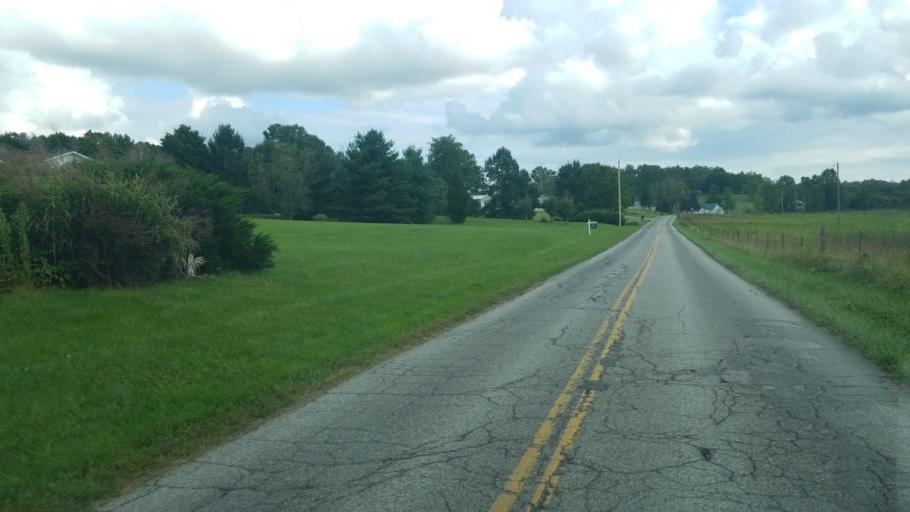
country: US
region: Ohio
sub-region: Jackson County
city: Oak Hill
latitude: 38.9311
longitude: -82.6042
